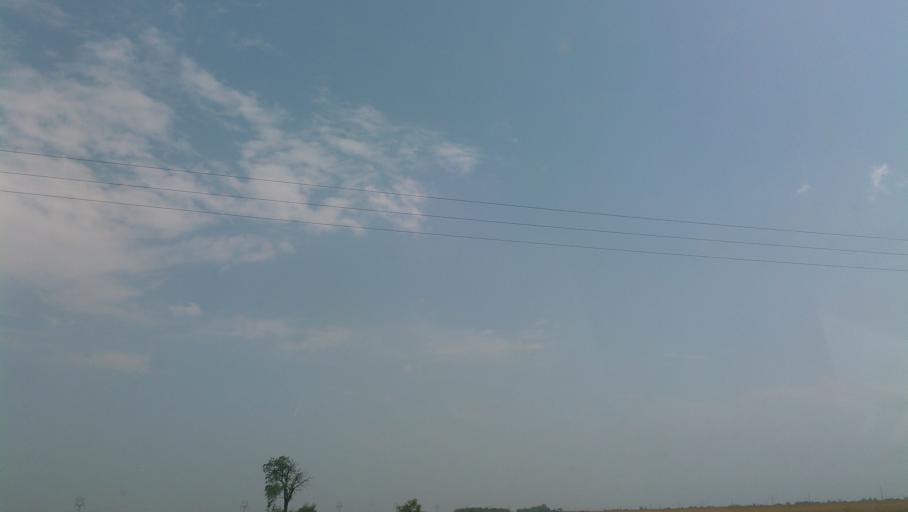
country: SK
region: Trnavsky
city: Samorin
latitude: 48.0946
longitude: 17.3630
